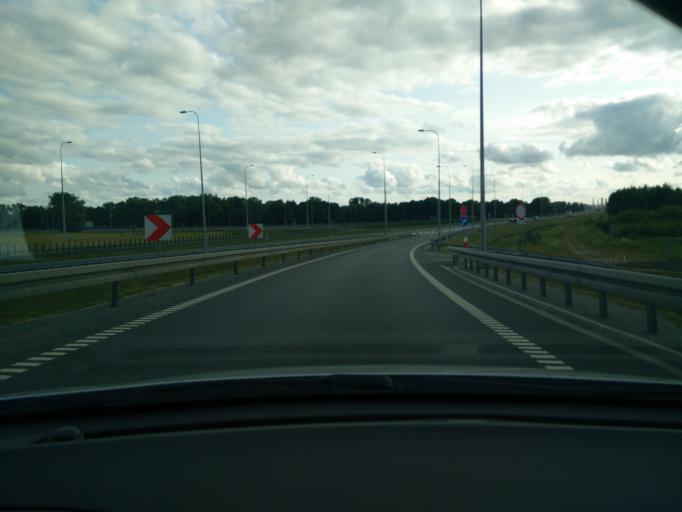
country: PL
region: Pomeranian Voivodeship
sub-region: Gdansk
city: Gdansk
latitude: 54.3198
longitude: 18.7041
